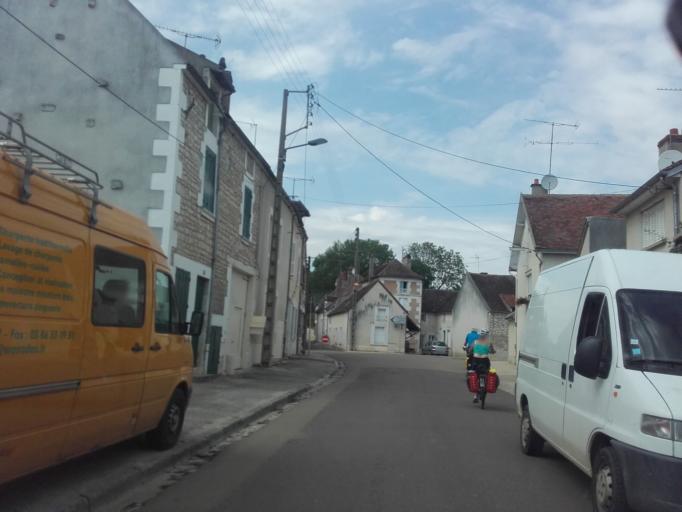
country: FR
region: Bourgogne
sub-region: Departement de l'Yonne
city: Chablis
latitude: 47.8106
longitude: 3.7995
